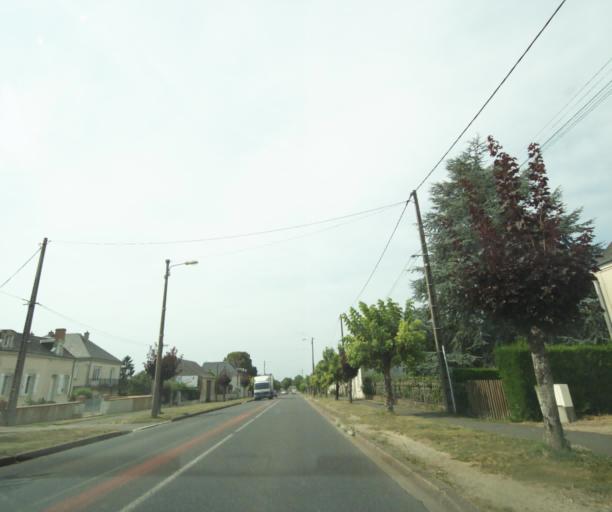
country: FR
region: Centre
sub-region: Departement d'Indre-et-Loire
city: Neuille-Pont-Pierre
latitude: 47.5488
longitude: 0.5509
